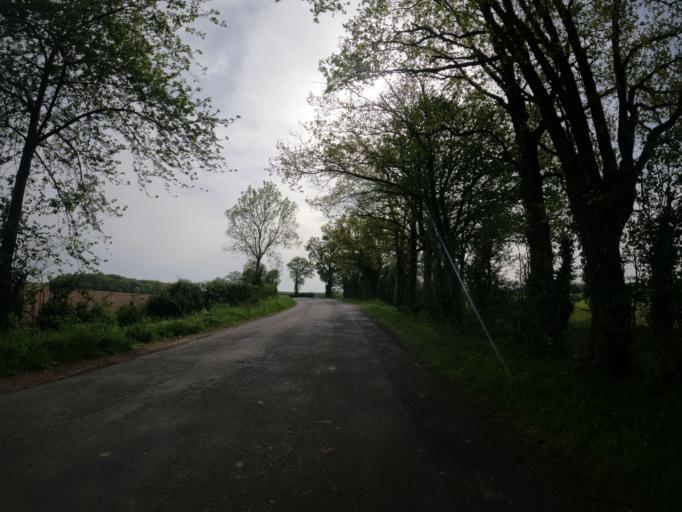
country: FR
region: Poitou-Charentes
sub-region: Departement des Deux-Sevres
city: Moncoutant
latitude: 46.6957
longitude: -0.5415
